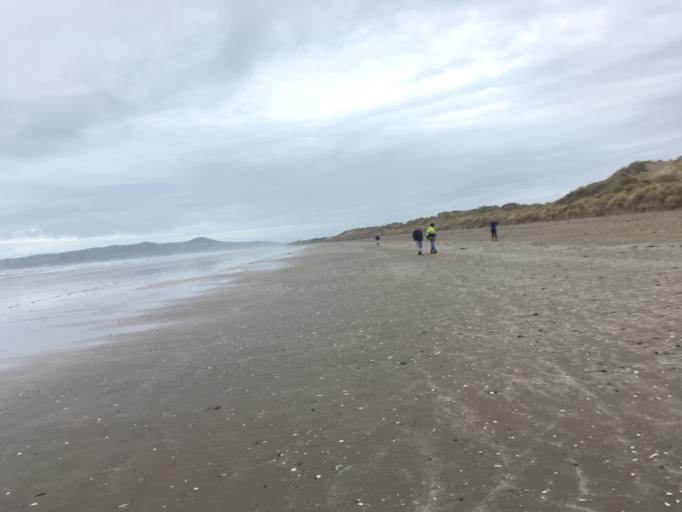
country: IE
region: Leinster
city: Portmarnock
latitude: 53.4213
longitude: -6.1215
